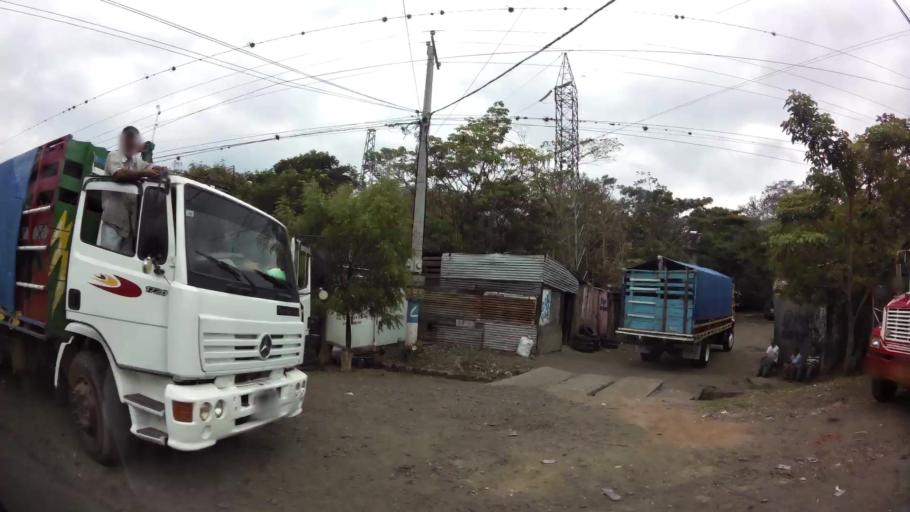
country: NI
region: Matagalpa
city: Matagalpa
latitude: 12.9372
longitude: -85.9104
